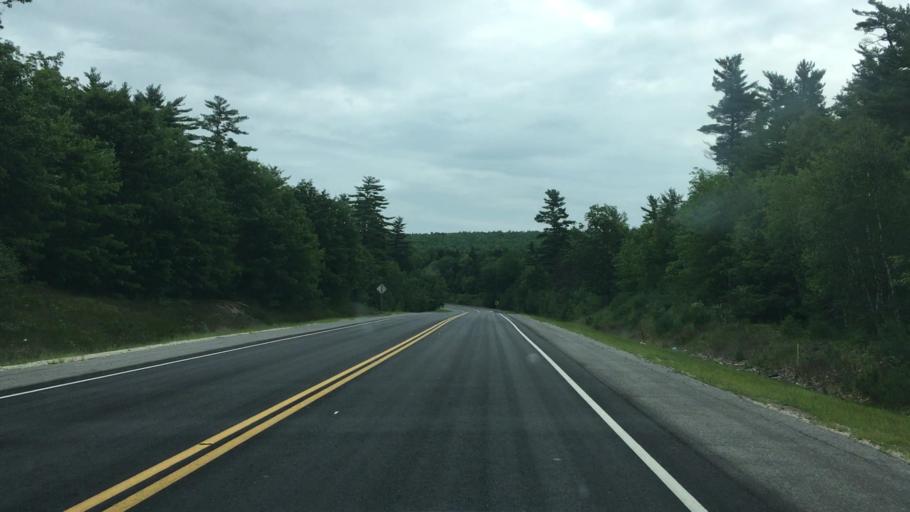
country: US
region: Maine
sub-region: Washington County
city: Cherryfield
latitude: 44.8806
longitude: -67.8618
